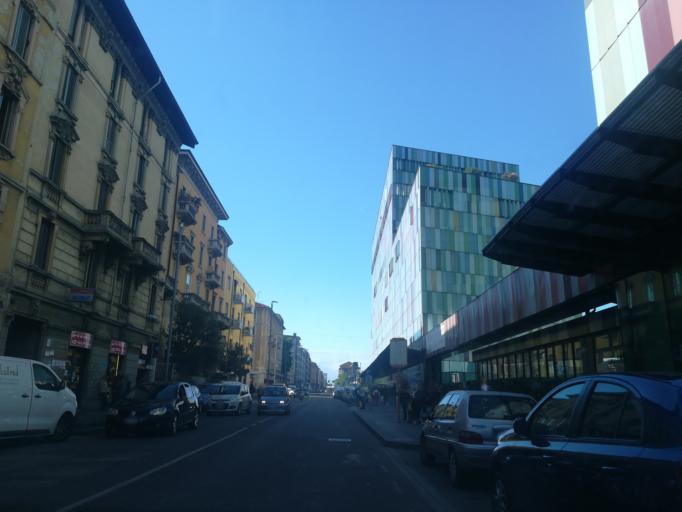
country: IT
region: Lombardy
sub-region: Citta metropolitana di Milano
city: Milano
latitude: 45.4998
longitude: 9.1836
